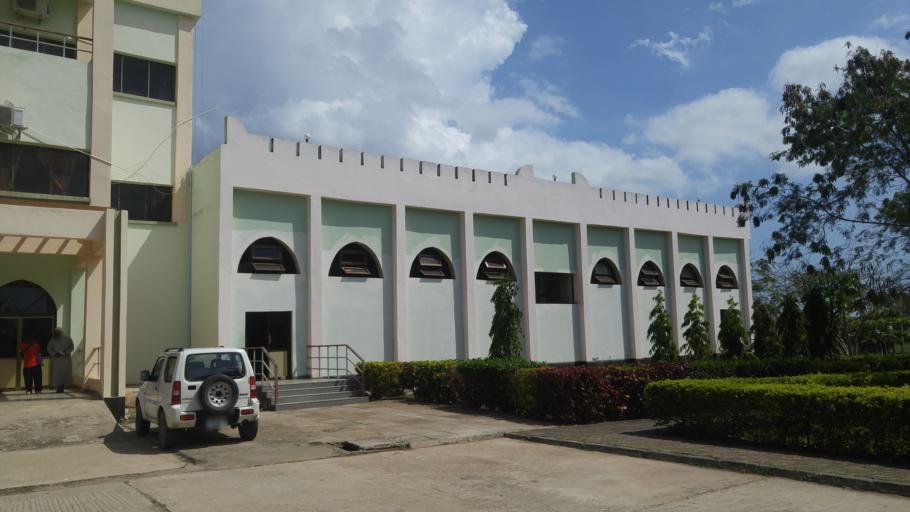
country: TZ
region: Zanzibar Central/South
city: Koani
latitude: -6.1991
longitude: 39.3075
